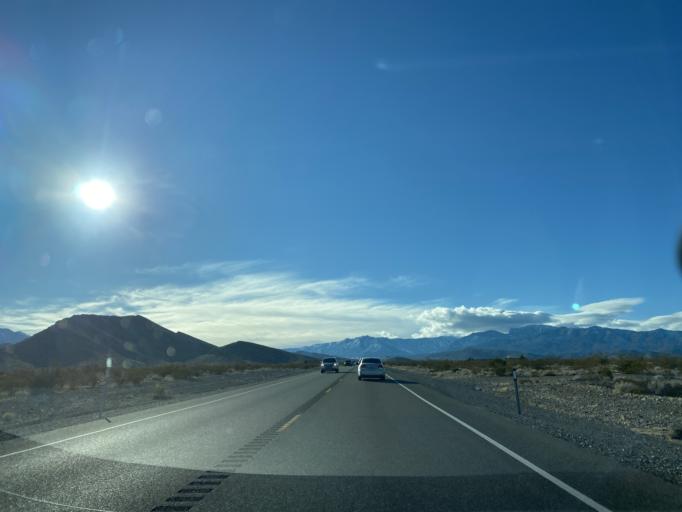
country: US
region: Nevada
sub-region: Clark County
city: Summerlin South
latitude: 36.3123
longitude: -115.3838
